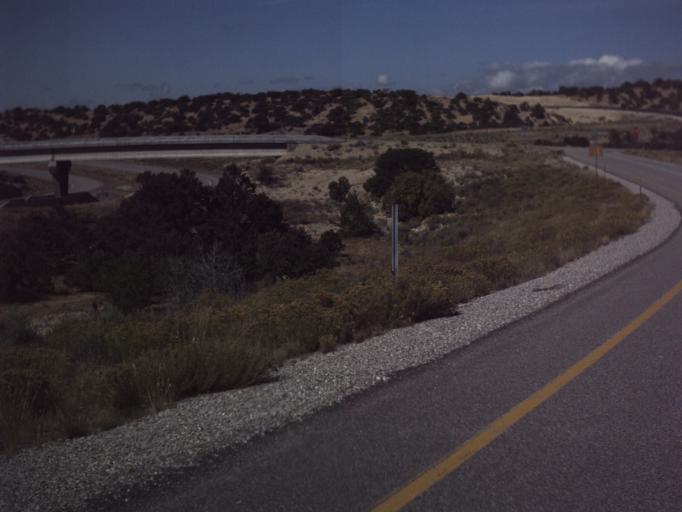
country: US
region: Utah
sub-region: Emery County
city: Ferron
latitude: 38.8557
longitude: -110.9116
